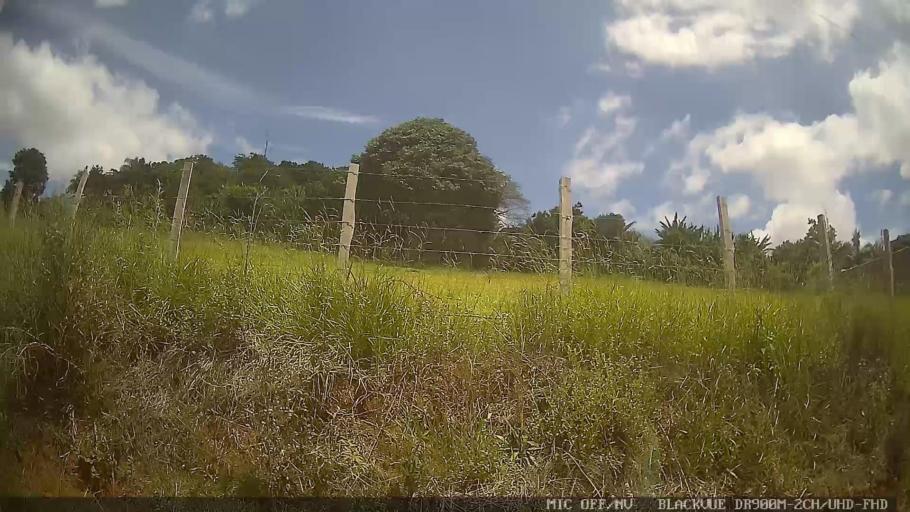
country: BR
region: Sao Paulo
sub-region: Braganca Paulista
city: Braganca Paulista
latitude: -23.0260
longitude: -46.5420
